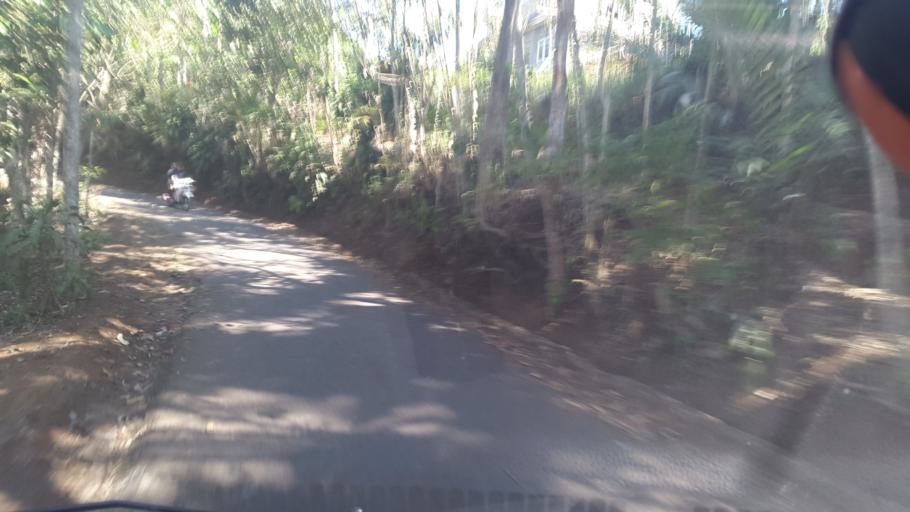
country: ID
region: West Java
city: Cicurug
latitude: -6.8489
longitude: 106.6993
